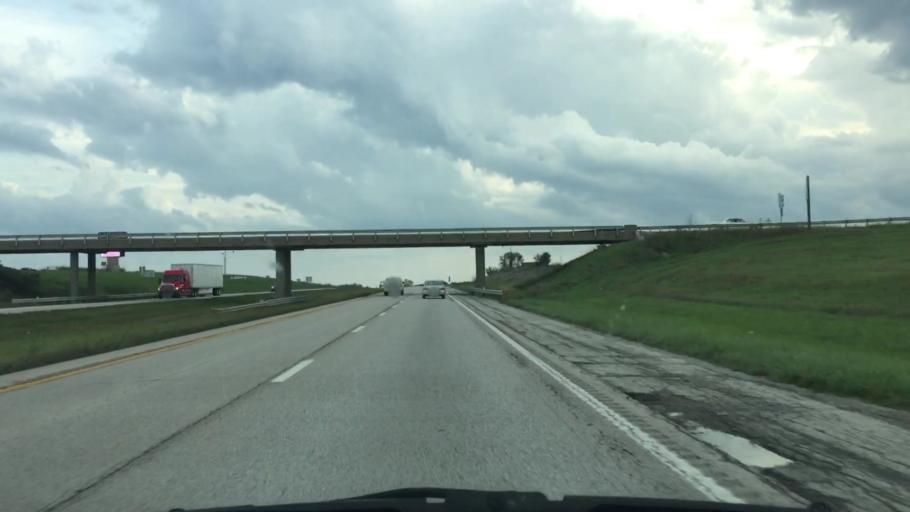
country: US
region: Missouri
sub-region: Clinton County
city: Cameron
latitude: 39.7323
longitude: -94.2207
